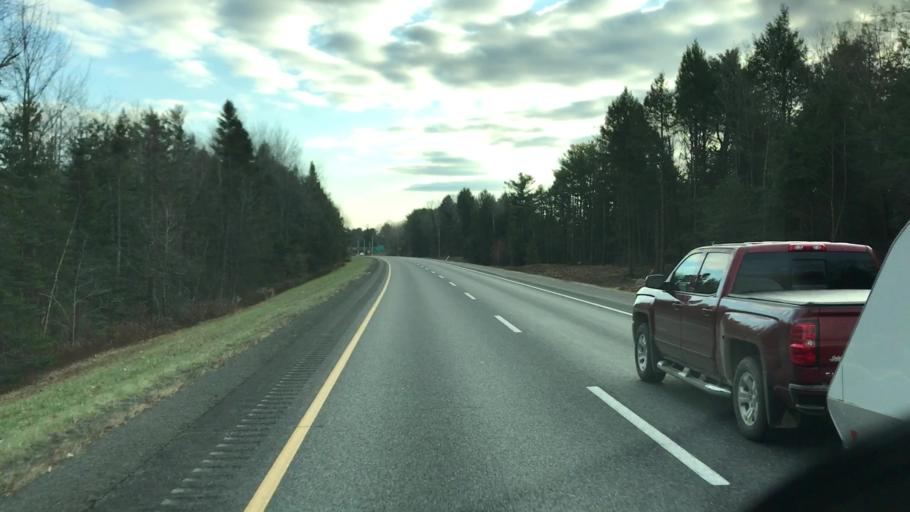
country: US
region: Maine
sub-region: Kennebec County
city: Oakland
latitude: 44.5139
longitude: -69.7026
